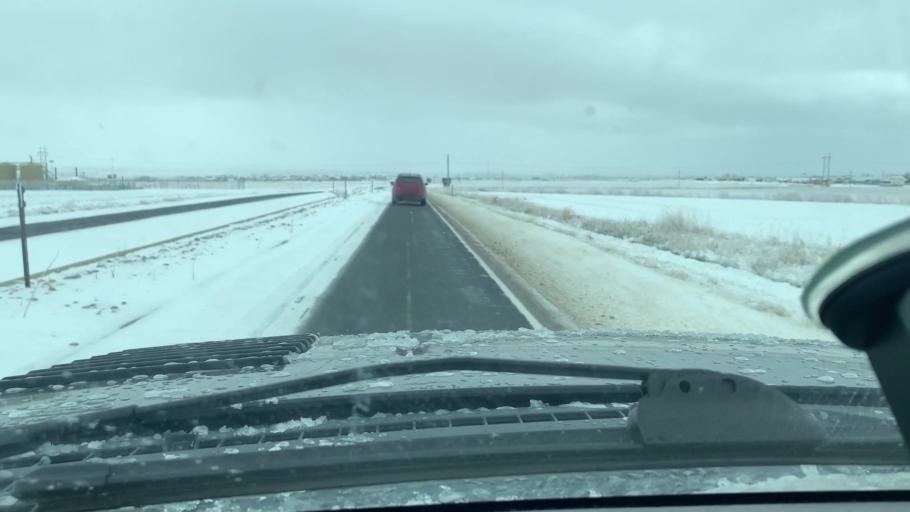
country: US
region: Colorado
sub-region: Weld County
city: Mead
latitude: 40.2004
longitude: -104.9702
